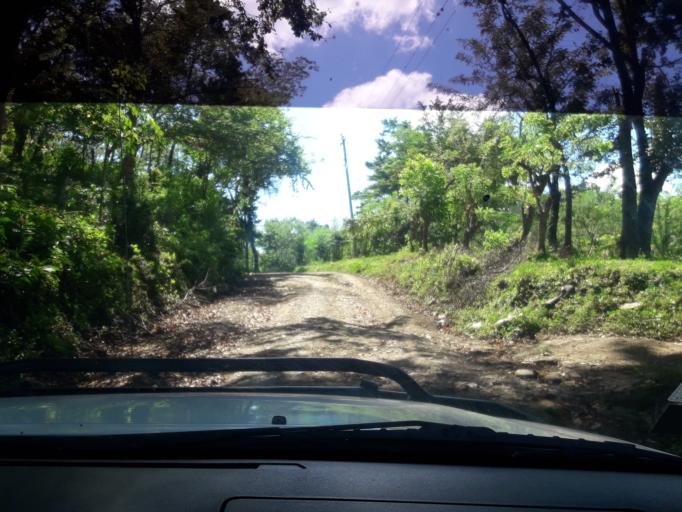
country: CR
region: Guanacaste
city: La Cruz
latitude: 11.2119
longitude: -85.6514
